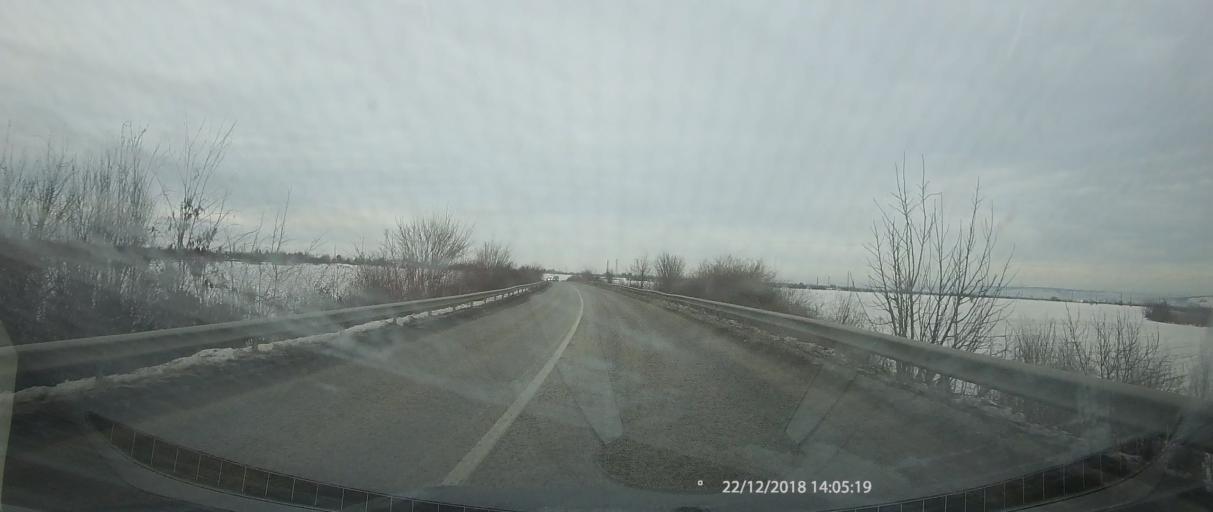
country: BG
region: Pleven
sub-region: Obshtina Dolni Dubnik
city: Dolni Dubnik
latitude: 43.4008
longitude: 24.4557
